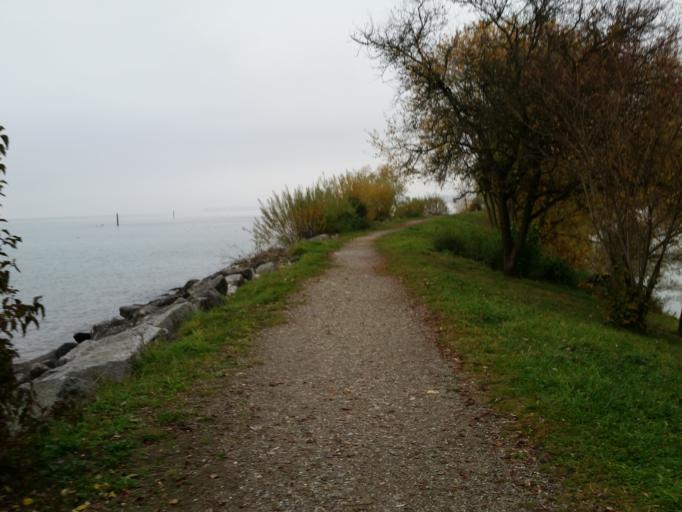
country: CH
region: Thurgau
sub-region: Arbon District
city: Romanshorn
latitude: 47.5640
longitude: 9.3839
